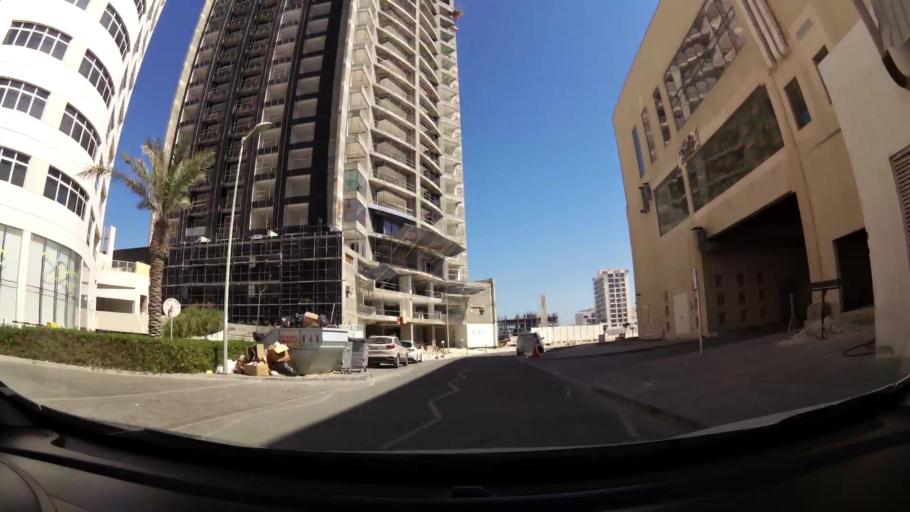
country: BH
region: Muharraq
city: Al Hadd
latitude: 26.2901
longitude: 50.6650
